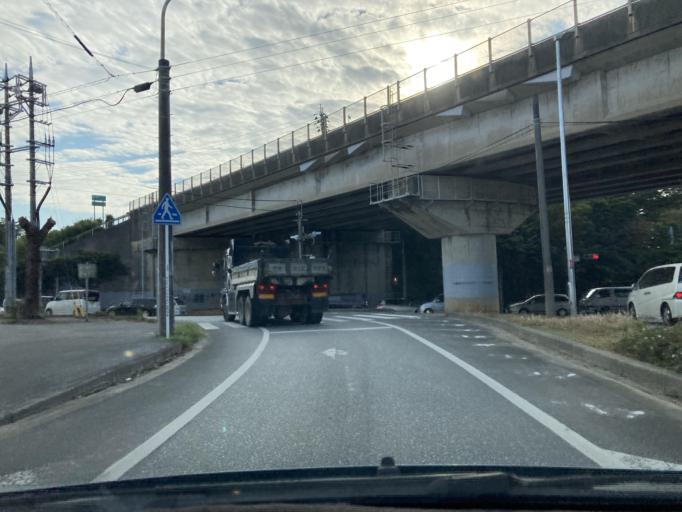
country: JP
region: Okinawa
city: Okinawa
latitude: 26.3565
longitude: 127.8046
